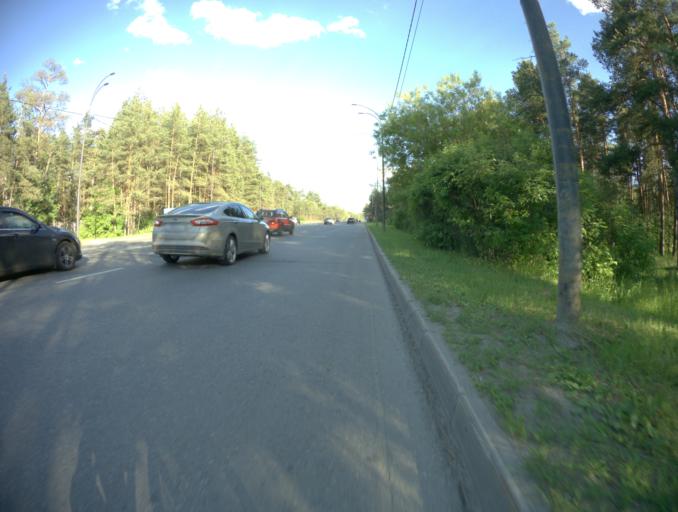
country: RU
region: Vladimir
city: Kommunar
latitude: 56.1000
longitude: 40.4414
